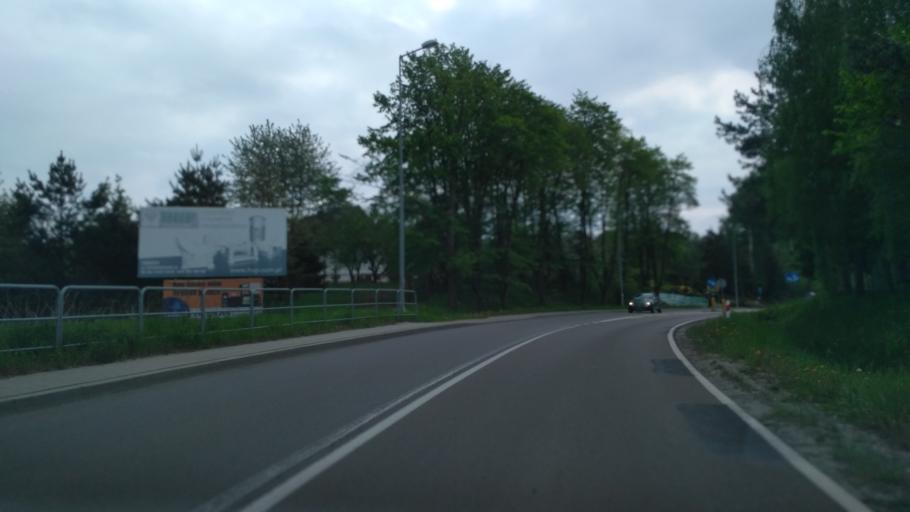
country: PL
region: Lesser Poland Voivodeship
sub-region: Powiat tarnowski
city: Tarnowiec
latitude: 49.9695
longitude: 20.9944
